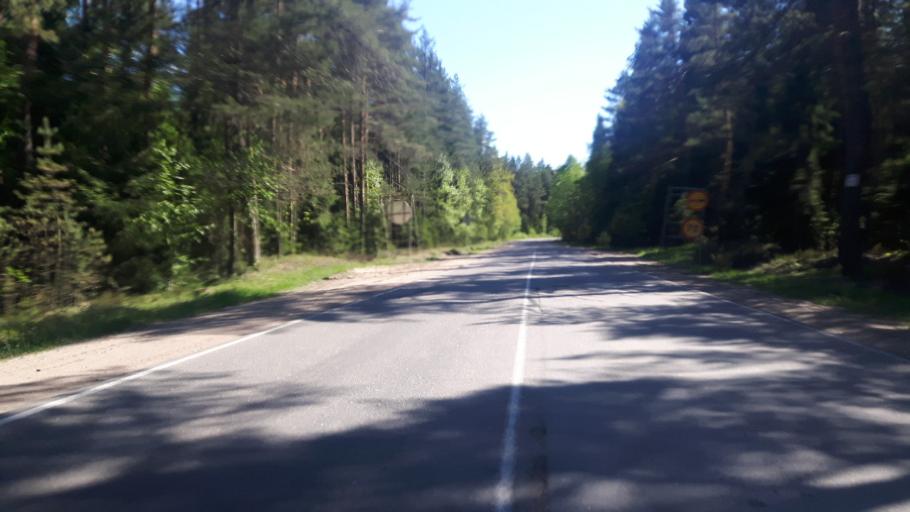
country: RU
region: Leningrad
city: Glebychevo
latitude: 60.2394
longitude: 29.0030
